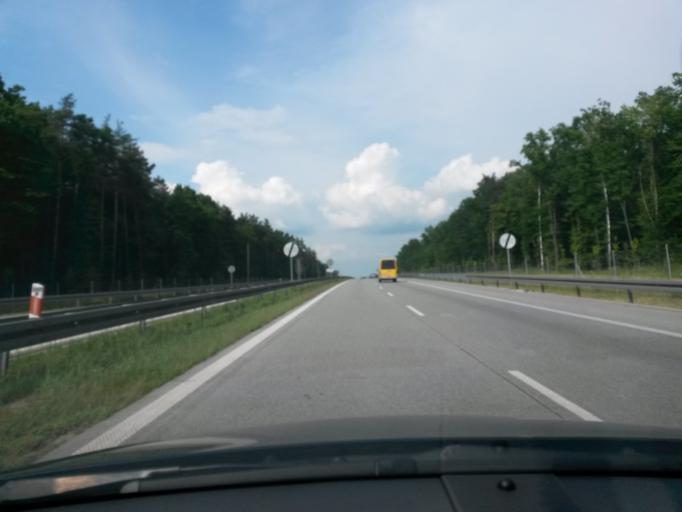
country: PL
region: Lodz Voivodeship
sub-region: Powiat tomaszowski
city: Lubochnia
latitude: 51.5815
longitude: 20.0317
